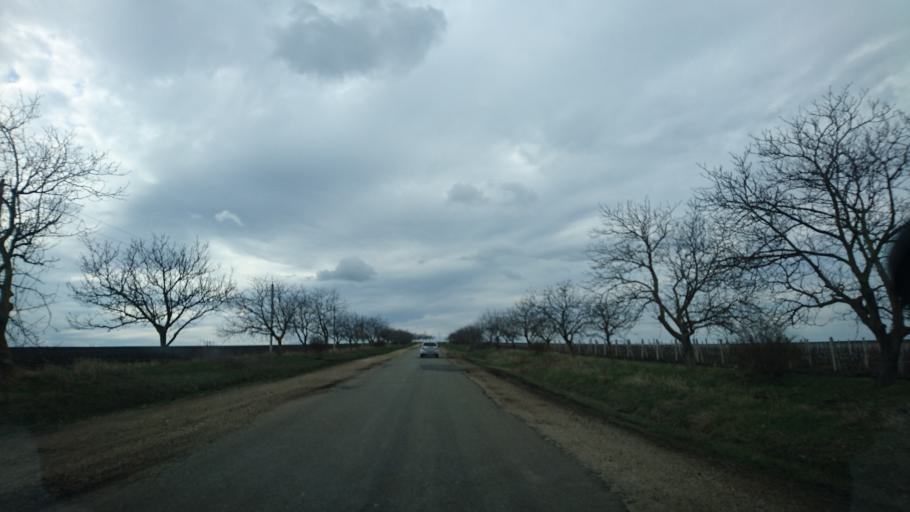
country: MD
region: Cantemir
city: Visniovca
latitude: 46.3175
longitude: 28.5509
